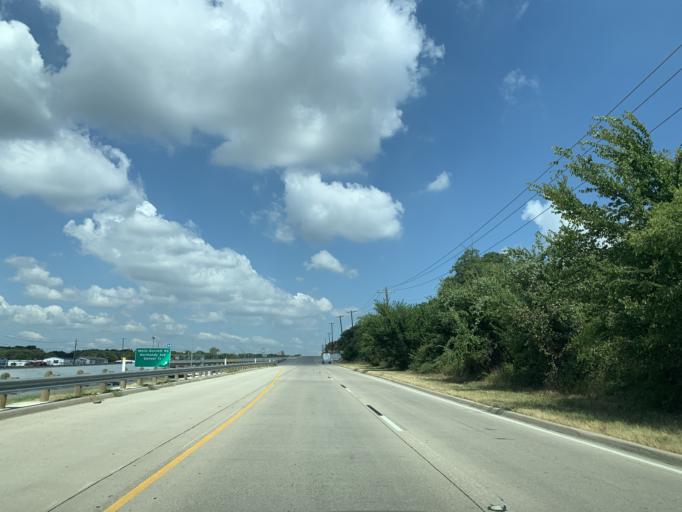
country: US
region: Texas
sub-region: Tarrant County
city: Lakeside
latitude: 32.8581
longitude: -97.5155
